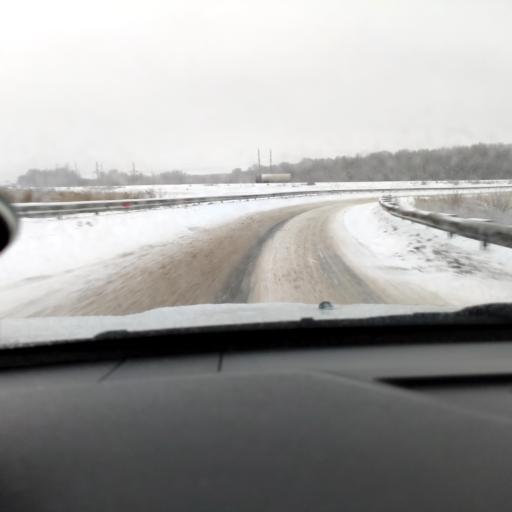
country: RU
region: Samara
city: Smyshlyayevka
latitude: 53.2620
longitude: 50.4731
